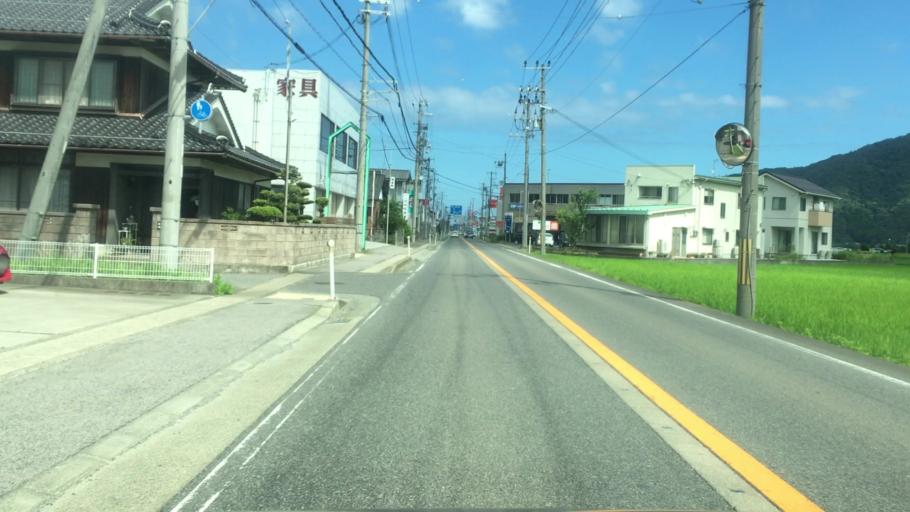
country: JP
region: Tottori
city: Tottori
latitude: 35.6124
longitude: 134.4684
